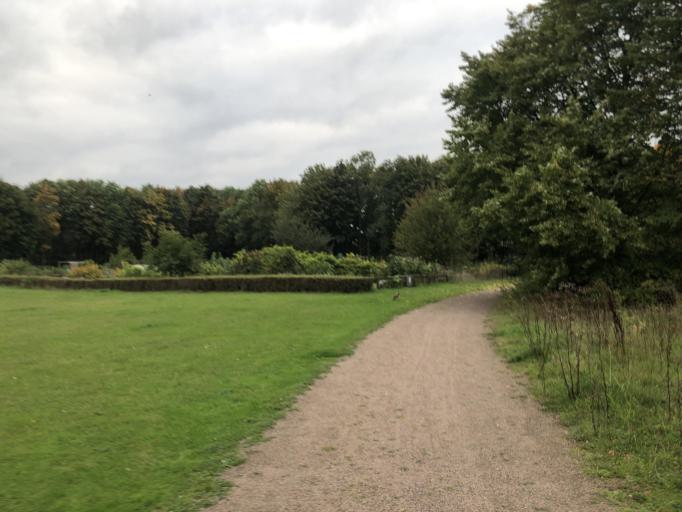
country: SE
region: Skane
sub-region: Burlovs Kommun
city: Arloev
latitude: 55.5965
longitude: 13.0725
